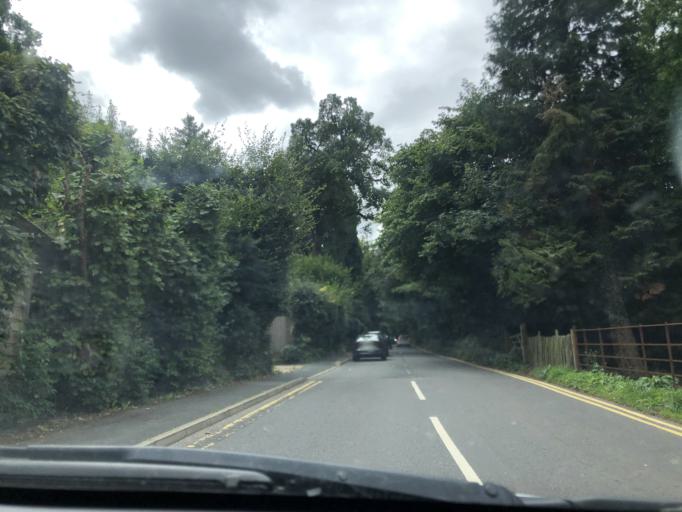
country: GB
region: England
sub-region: Kent
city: Westerham
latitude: 51.2649
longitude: 0.0781
